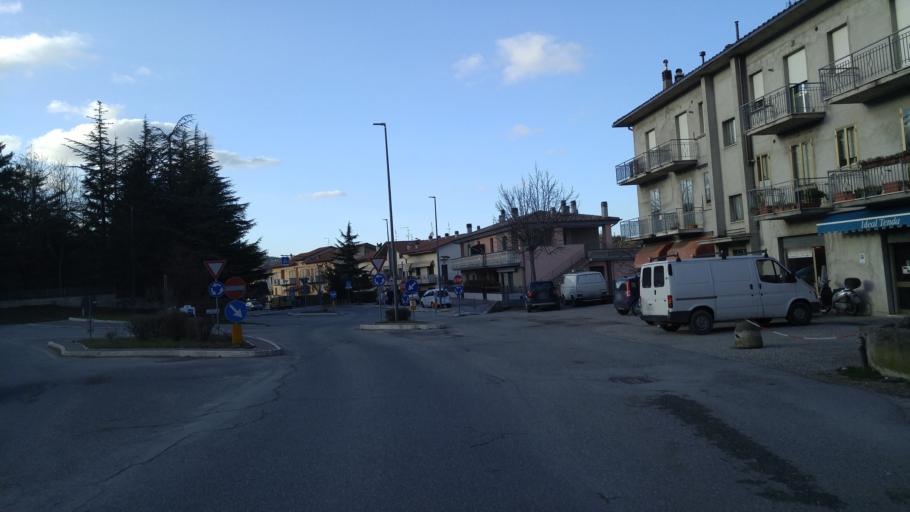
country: IT
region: The Marches
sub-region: Provincia di Pesaro e Urbino
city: Cagli
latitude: 43.5455
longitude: 12.6605
